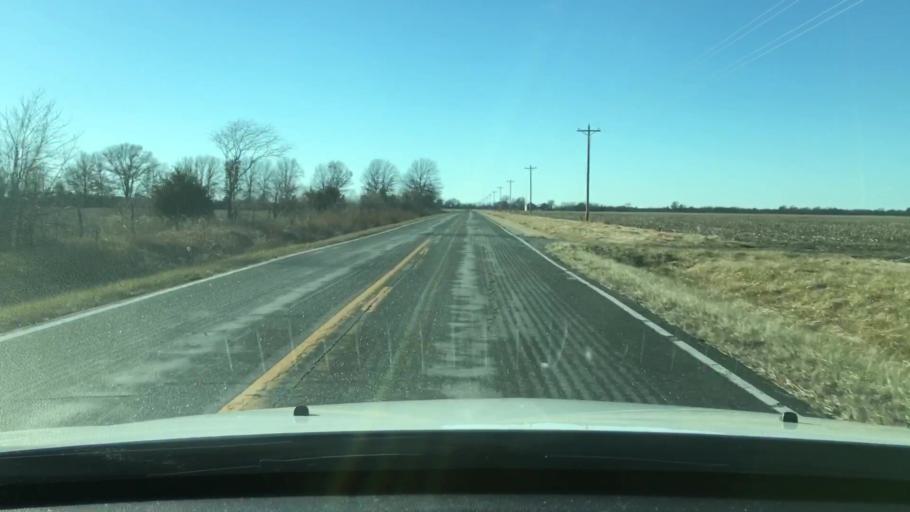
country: US
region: Missouri
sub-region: Audrain County
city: Mexico
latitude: 39.2816
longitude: -91.7264
